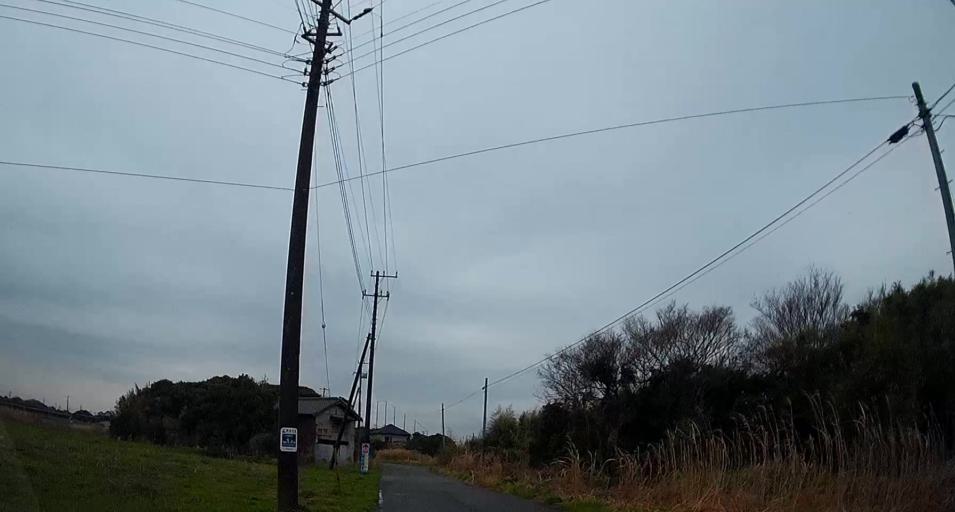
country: JP
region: Chiba
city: Kisarazu
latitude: 35.4104
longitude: 139.9046
